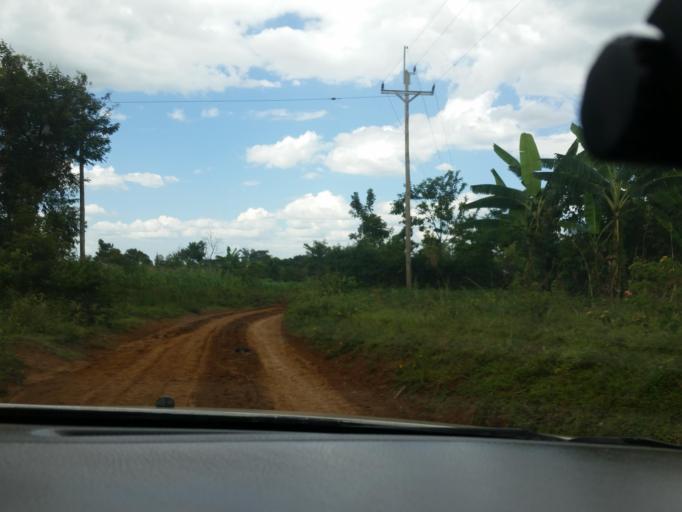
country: KE
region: Siaya
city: Yala
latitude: 0.0989
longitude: 34.4128
